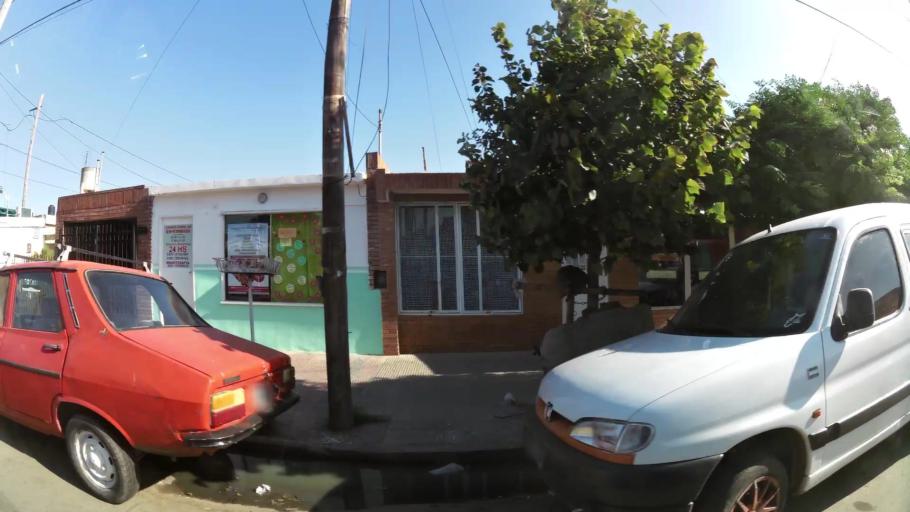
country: AR
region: Cordoba
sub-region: Departamento de Capital
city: Cordoba
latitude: -31.4758
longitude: -64.2196
